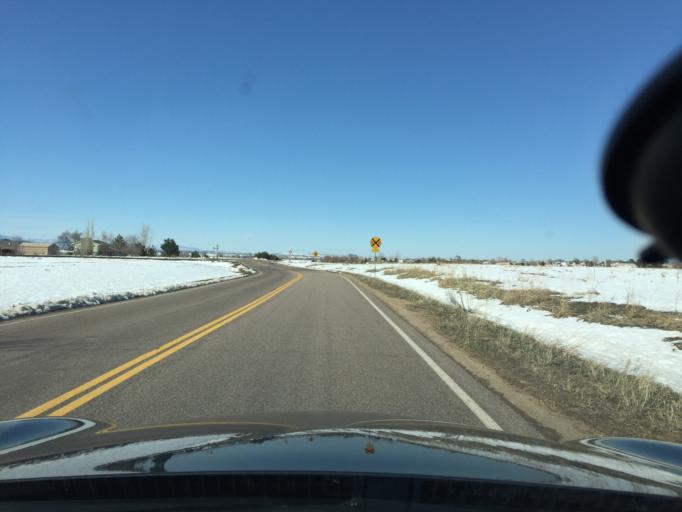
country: US
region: Colorado
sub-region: Boulder County
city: Erie
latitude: 40.0607
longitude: -105.0370
